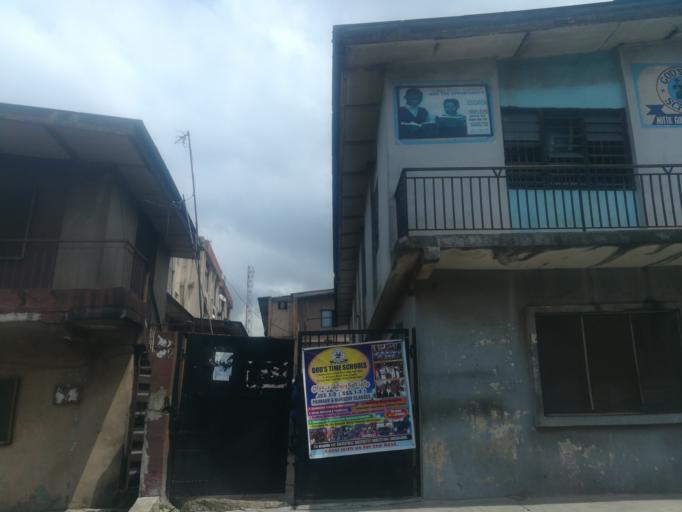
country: NG
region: Lagos
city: Ojota
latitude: 6.5997
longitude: 3.3901
